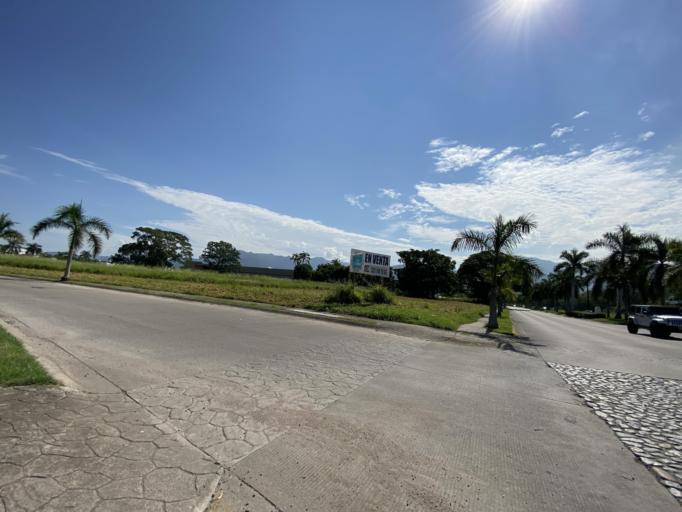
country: MX
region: Jalisco
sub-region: Puerto Vallarta
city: Puerto Vallarta
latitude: 20.6411
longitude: -105.2259
